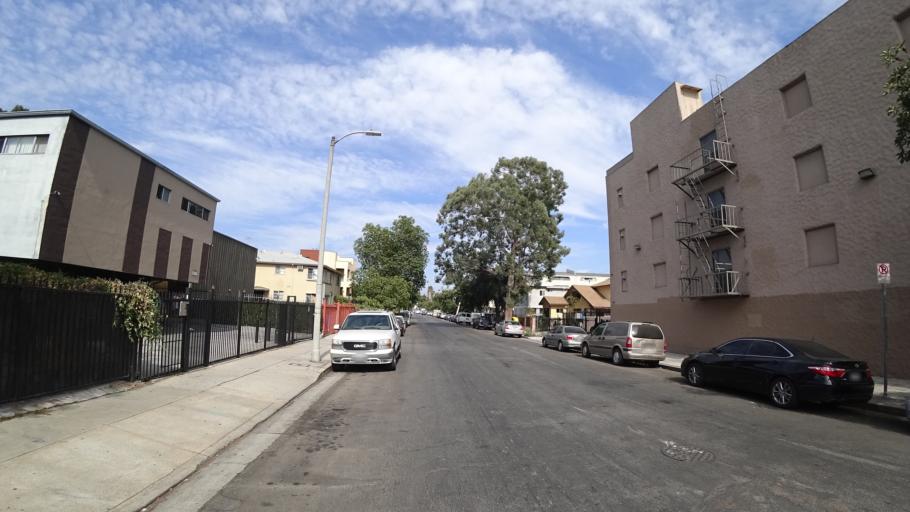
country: US
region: California
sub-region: Los Angeles County
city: Hollywood
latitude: 34.0918
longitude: -118.3177
